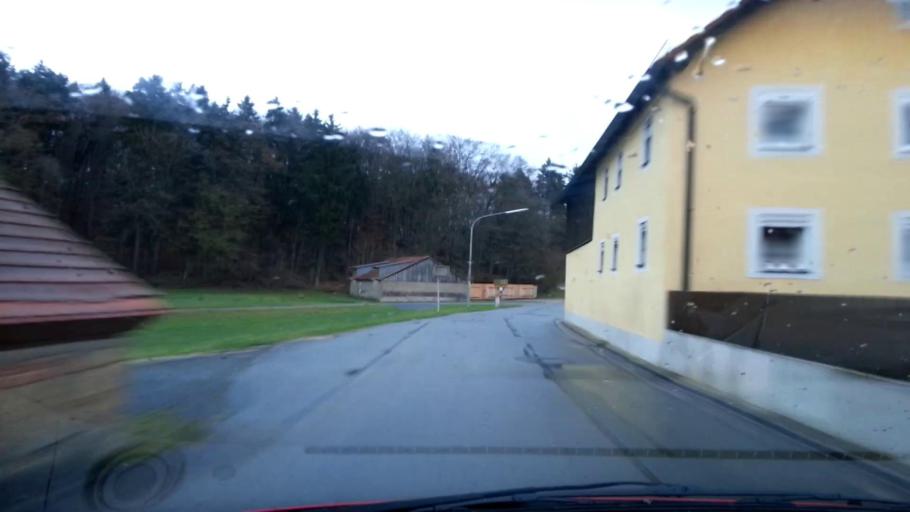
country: DE
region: Bavaria
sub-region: Upper Franconia
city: Aufsess
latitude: 49.9308
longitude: 11.2046
